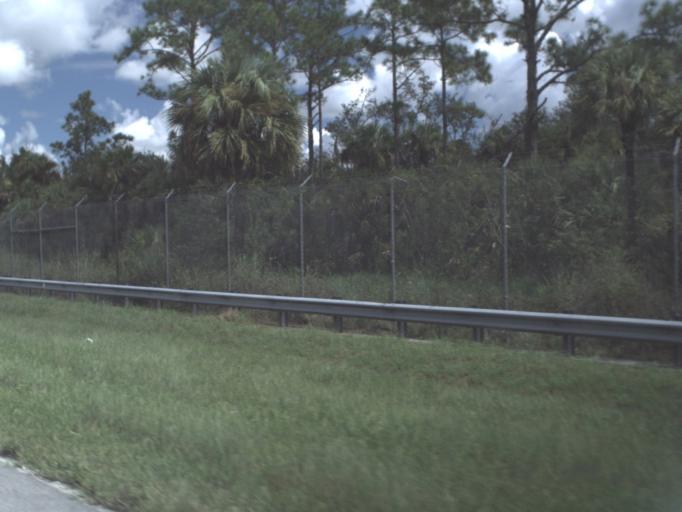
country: US
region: Florida
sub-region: Collier County
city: Immokalee
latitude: 26.1729
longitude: -81.3455
